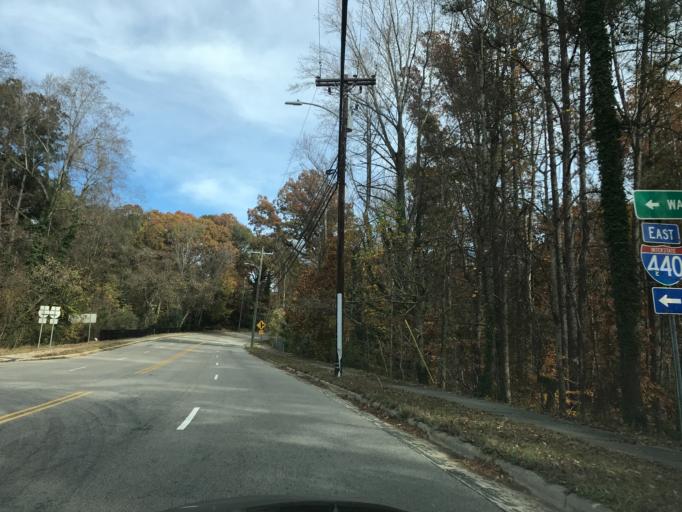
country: US
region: North Carolina
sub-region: Wake County
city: West Raleigh
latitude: 35.8154
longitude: -78.6885
